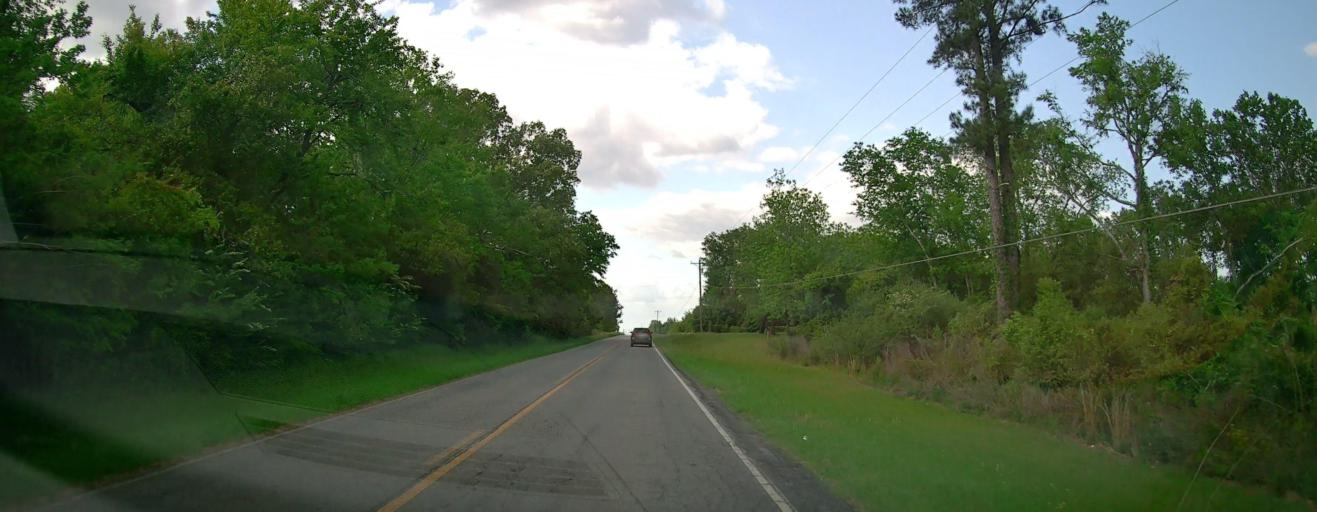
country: US
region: Georgia
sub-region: Laurens County
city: East Dublin
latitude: 32.5978
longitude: -82.8659
